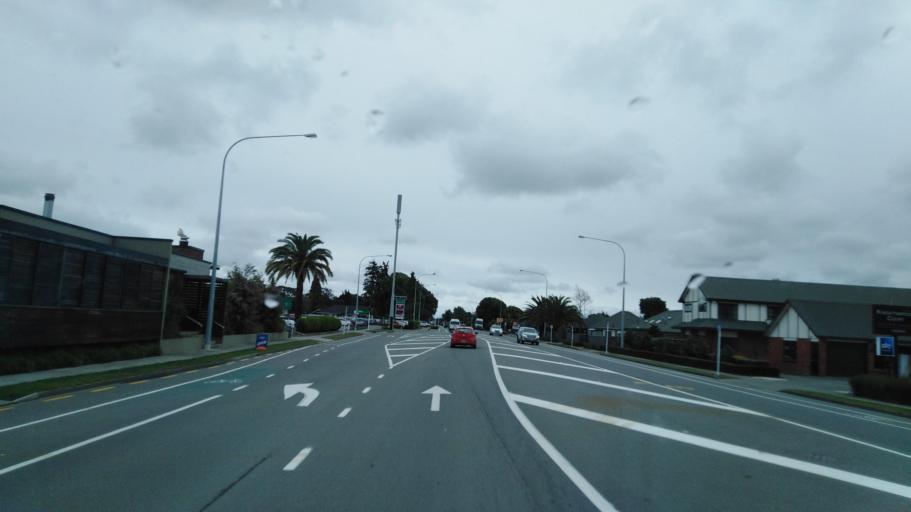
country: NZ
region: Marlborough
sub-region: Marlborough District
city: Blenheim
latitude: -41.5091
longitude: 173.9370
